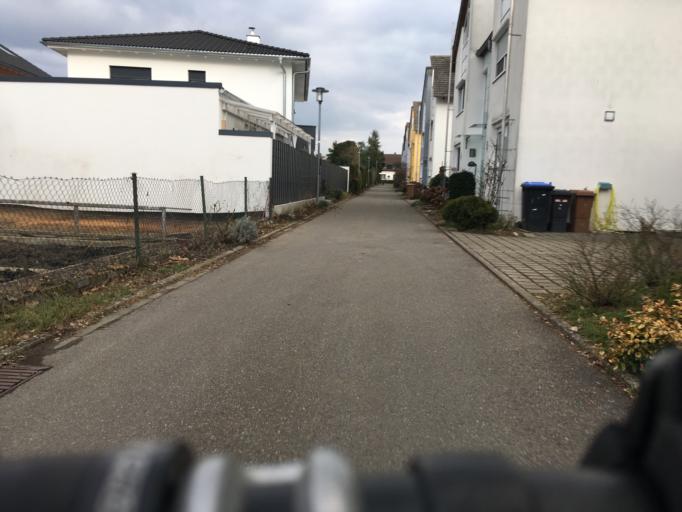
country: DE
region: Baden-Wuerttemberg
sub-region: Freiburg Region
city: Gottmadingen
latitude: 47.7289
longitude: 8.7771
